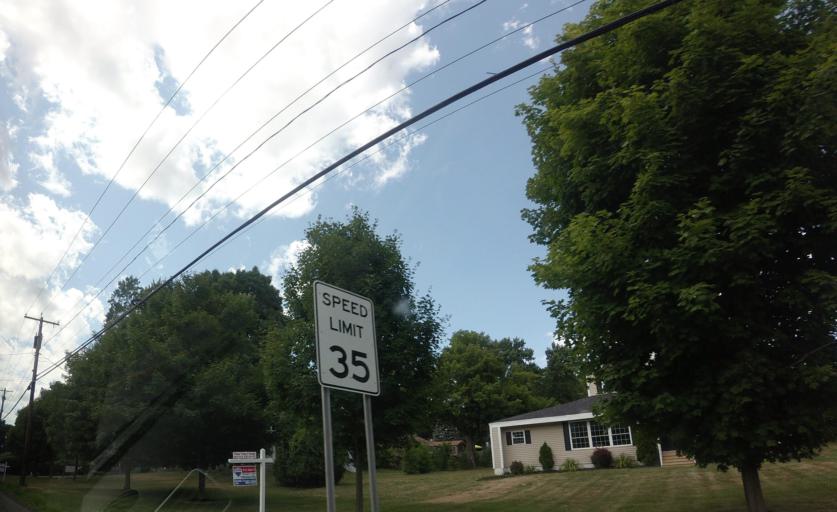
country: US
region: New York
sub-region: Onondaga County
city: Westvale
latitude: 43.0470
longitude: -76.2139
